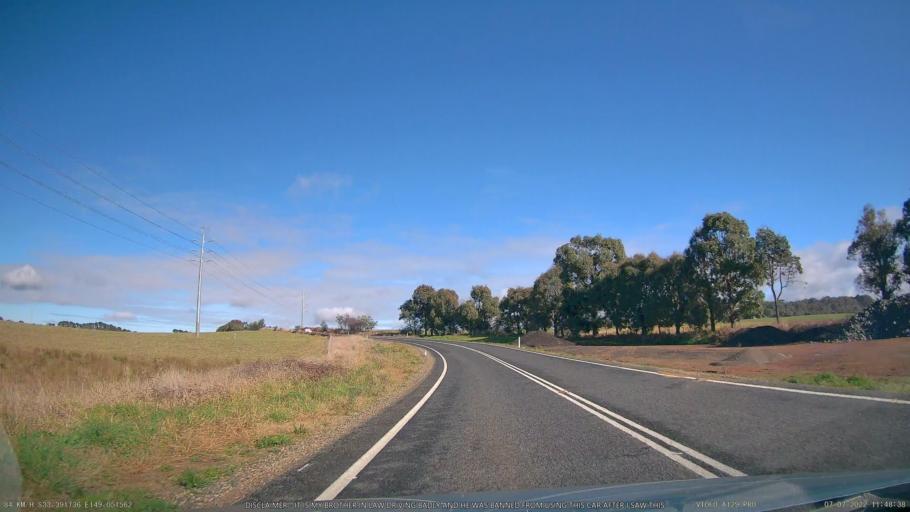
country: AU
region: New South Wales
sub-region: Orange Municipality
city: Orange
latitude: -33.3919
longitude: 149.0509
